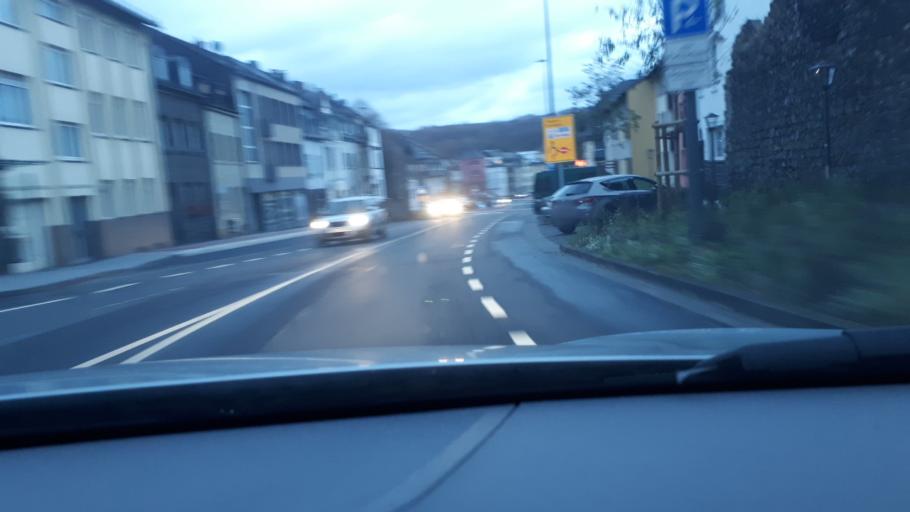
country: DE
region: Rheinland-Pfalz
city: Mayen
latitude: 50.3282
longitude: 7.2184
